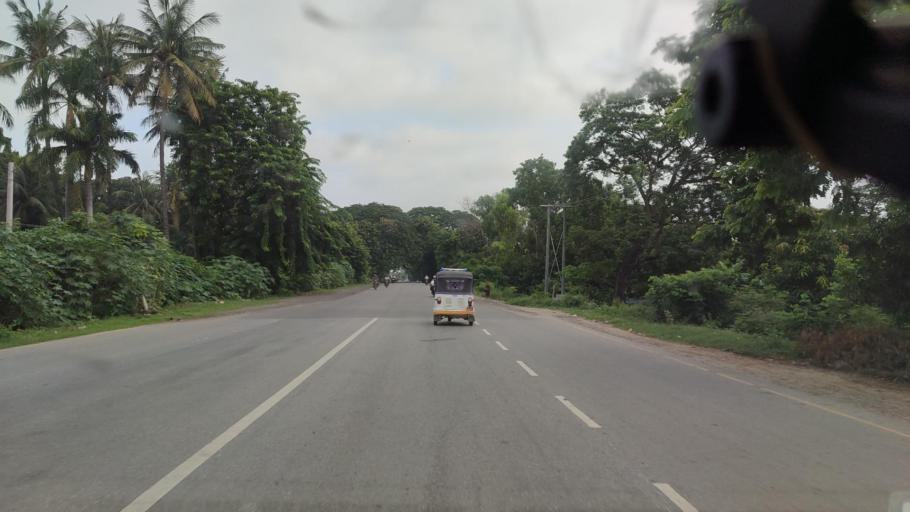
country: MM
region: Mandalay
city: Mandalay
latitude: 22.0889
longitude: 96.1466
